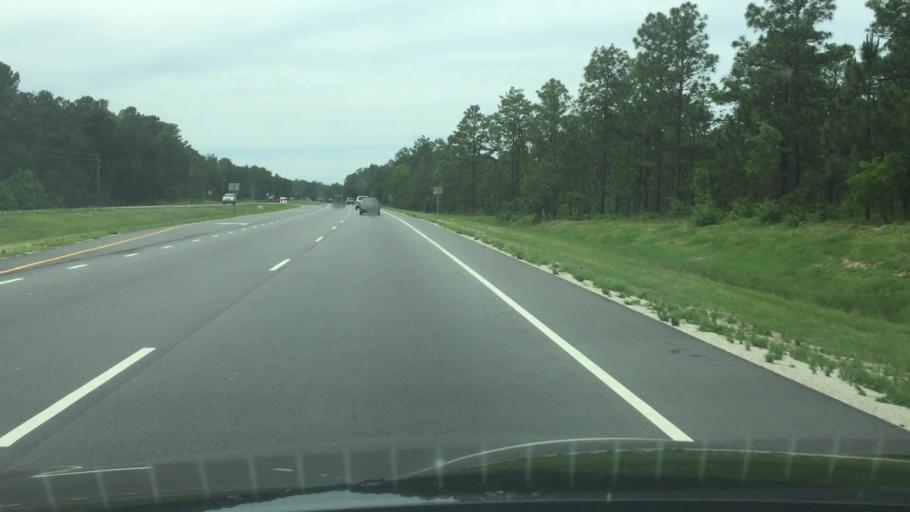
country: US
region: North Carolina
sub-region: Cumberland County
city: Spring Lake
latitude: 35.2270
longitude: -79.0110
